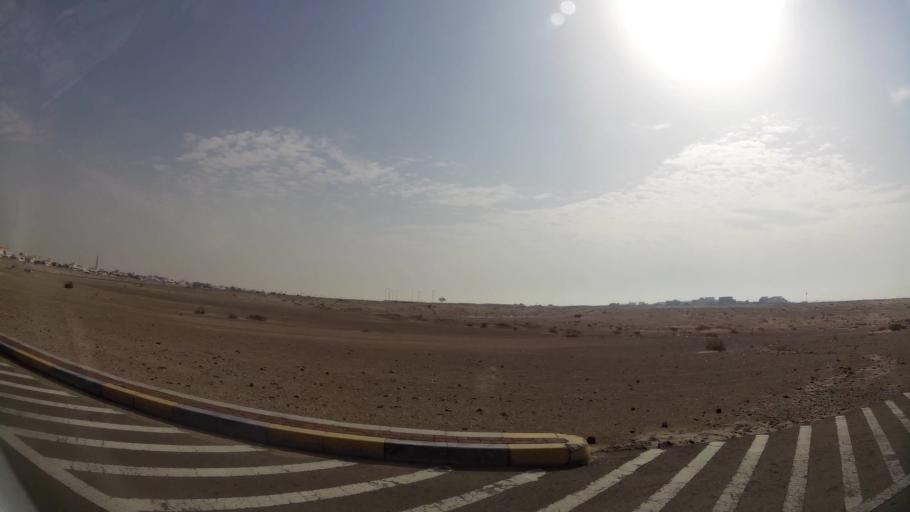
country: AE
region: Abu Dhabi
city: Abu Dhabi
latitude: 24.2716
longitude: 54.6840
